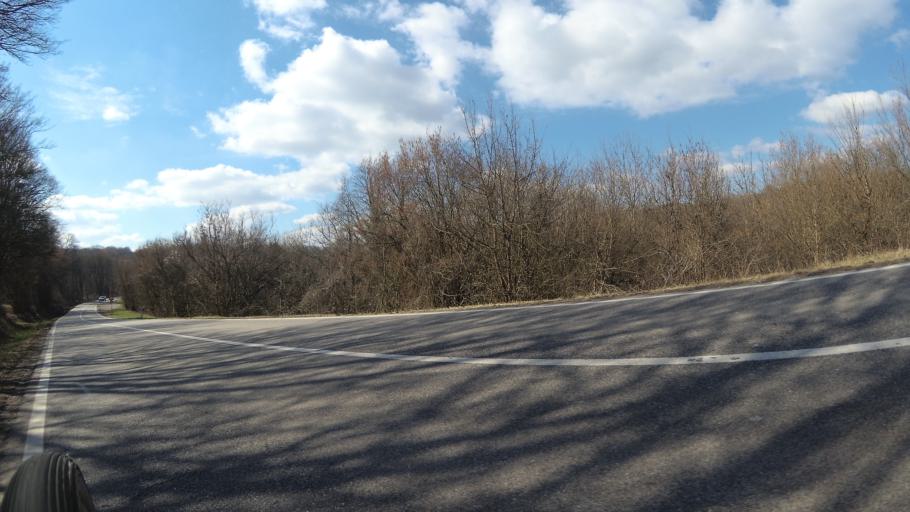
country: DE
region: Saarland
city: Rehlingen-Siersburg
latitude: 49.3570
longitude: 6.6432
